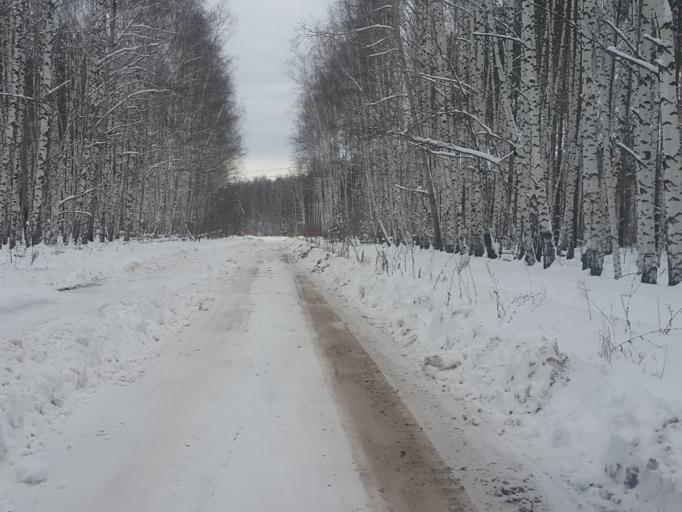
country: RU
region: Tambov
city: Platonovka
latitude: 52.8887
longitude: 41.8536
